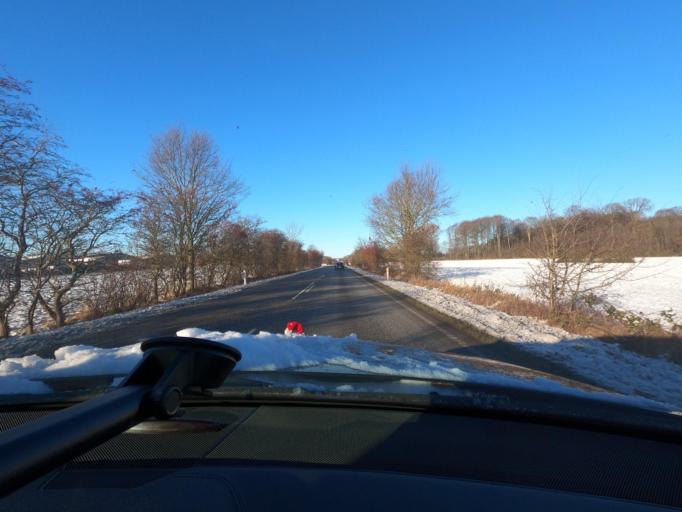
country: DK
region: South Denmark
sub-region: Sonderborg Kommune
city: Horuphav
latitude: 54.9139
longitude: 9.9108
